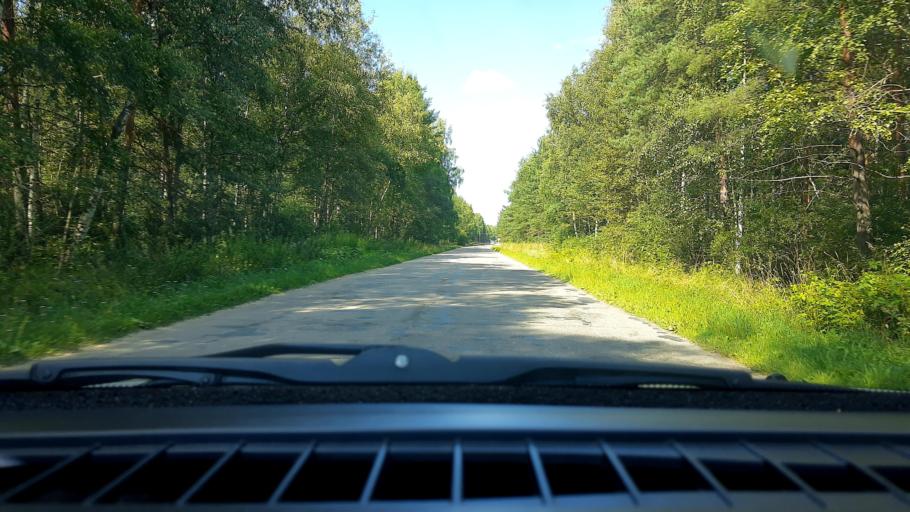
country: RU
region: Nizjnij Novgorod
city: Babino
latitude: 56.3284
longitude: 43.6342
